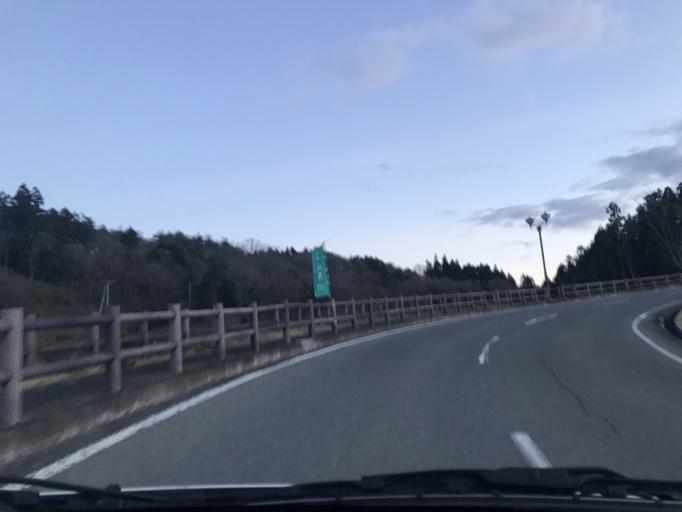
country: JP
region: Iwate
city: Ichinoseki
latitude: 38.8325
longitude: 141.0848
